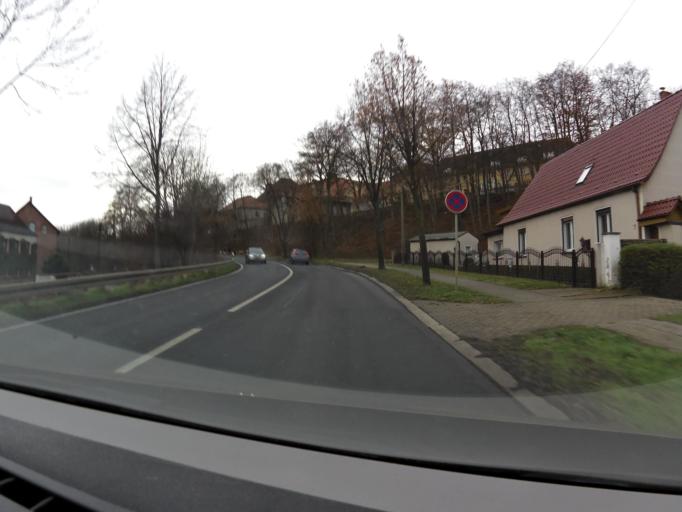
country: DE
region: Saxony-Anhalt
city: Aschersleben
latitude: 51.7480
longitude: 11.4588
